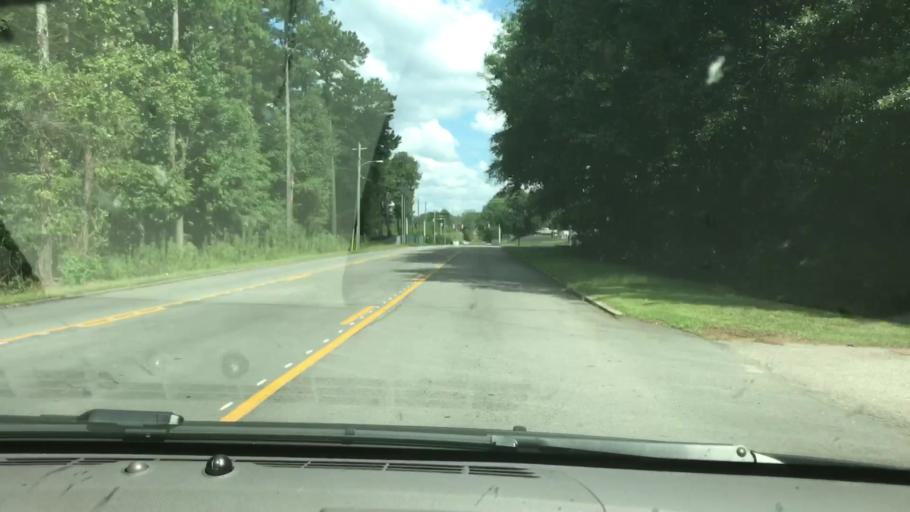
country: US
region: Georgia
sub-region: Troup County
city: La Grange
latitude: 33.0104
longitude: -85.0575
